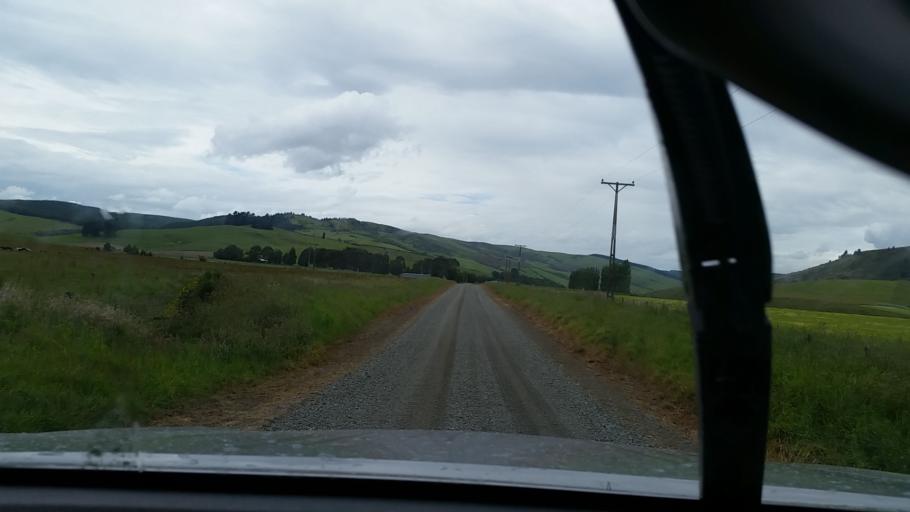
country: NZ
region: Southland
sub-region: Southland District
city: Winton
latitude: -45.9452
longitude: 168.1471
